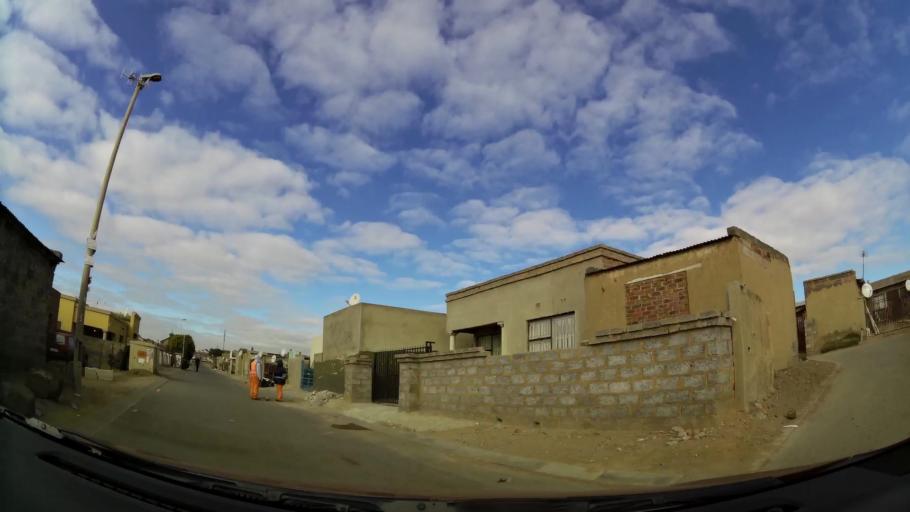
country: ZA
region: Gauteng
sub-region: City of Johannesburg Metropolitan Municipality
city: Modderfontein
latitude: -26.0368
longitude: 28.1818
